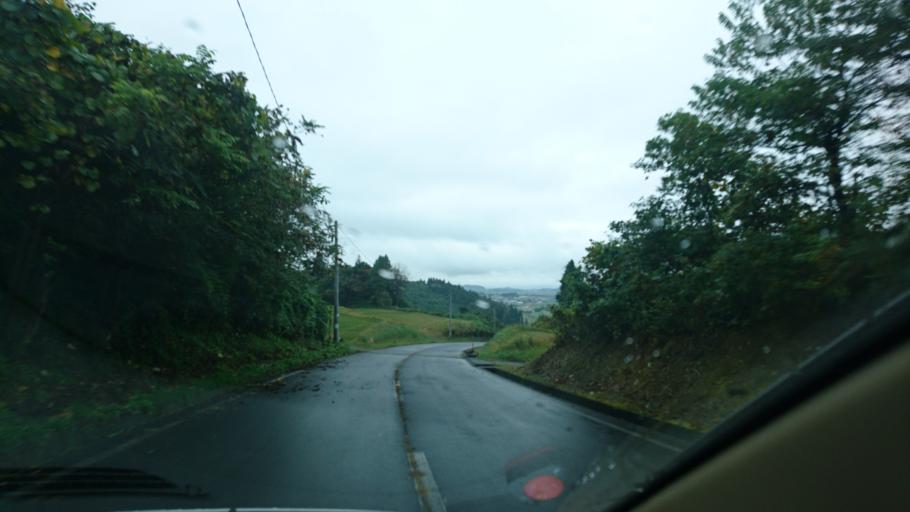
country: JP
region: Iwate
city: Ichinoseki
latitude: 38.9687
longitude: 141.1027
